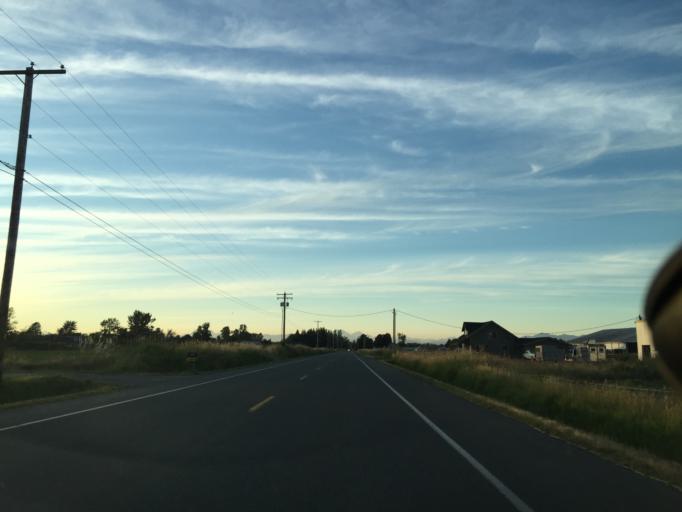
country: US
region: Washington
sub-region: Whatcom County
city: Everson
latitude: 48.9285
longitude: -122.3424
